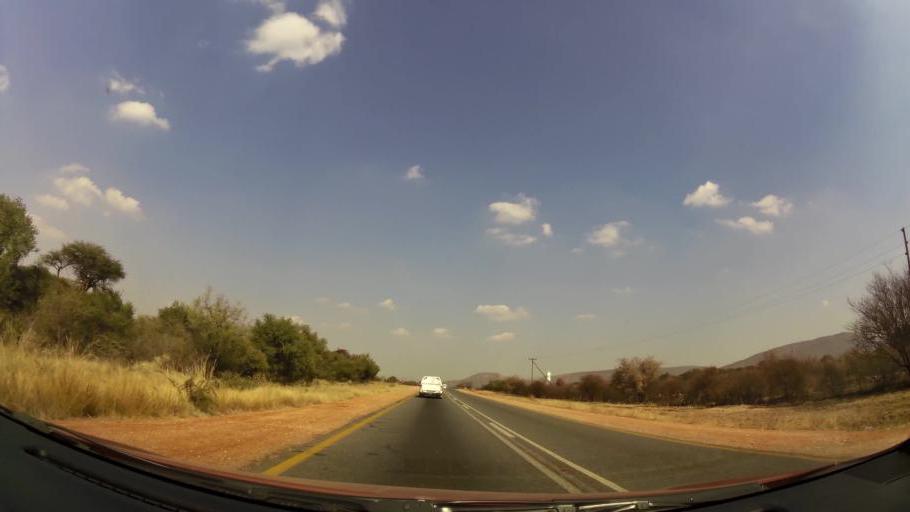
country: ZA
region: North-West
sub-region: Bojanala Platinum District Municipality
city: Mogwase
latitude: -25.4708
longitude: 27.0872
